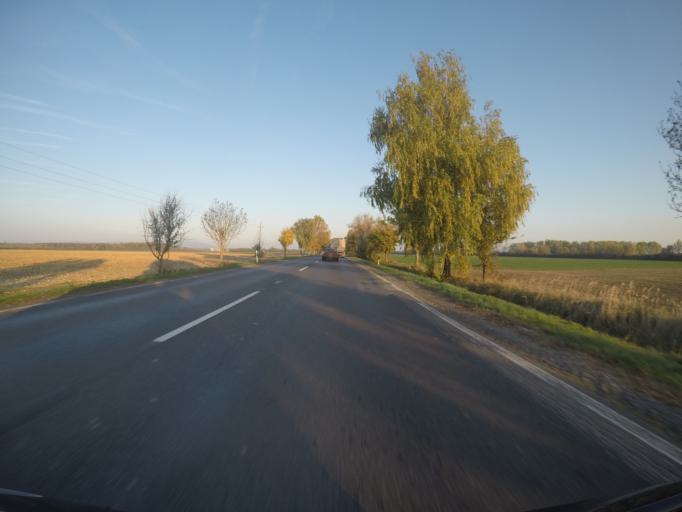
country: HU
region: Baranya
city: Szentlorinc
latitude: 46.0389
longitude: 17.9349
